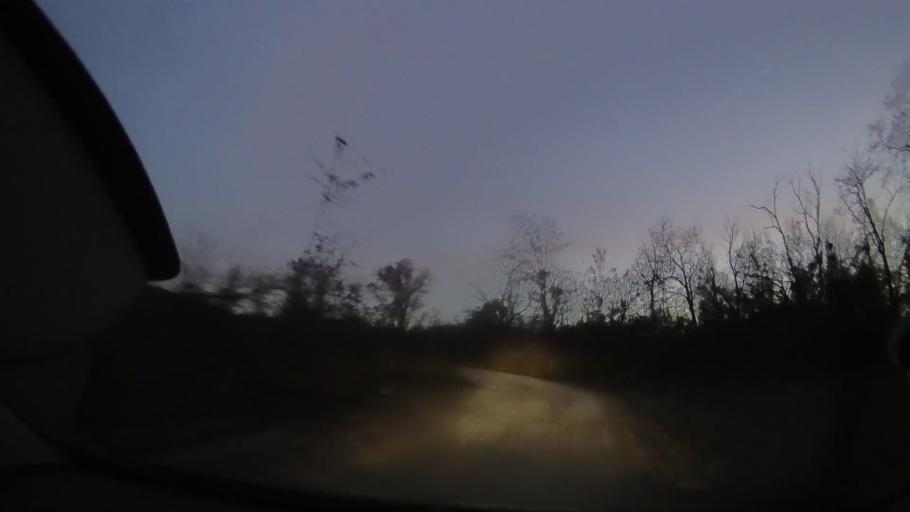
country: RO
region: Bihor
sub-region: Comuna Tetchea
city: Hotar
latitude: 47.0037
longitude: 22.3093
